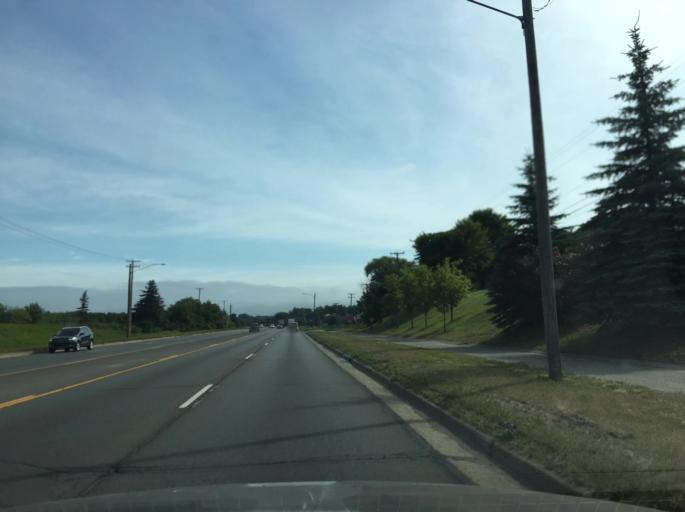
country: US
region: Michigan
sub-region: Grand Traverse County
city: Traverse City
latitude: 44.7449
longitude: -85.6394
